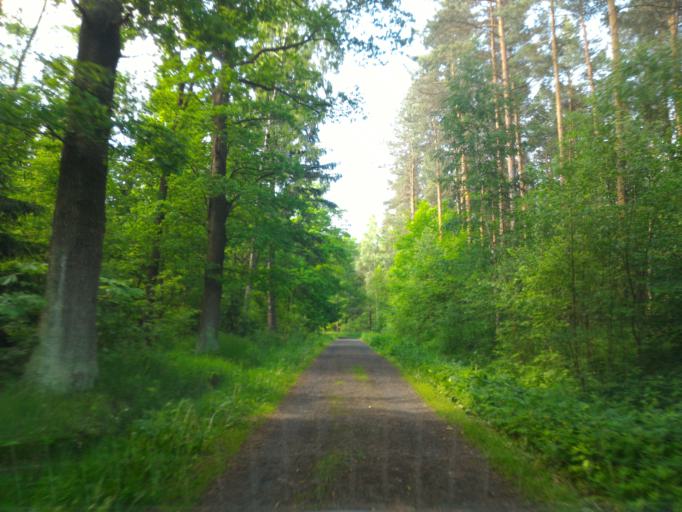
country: DE
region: Saxony
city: Grossschonau
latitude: 50.8768
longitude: 14.6659
